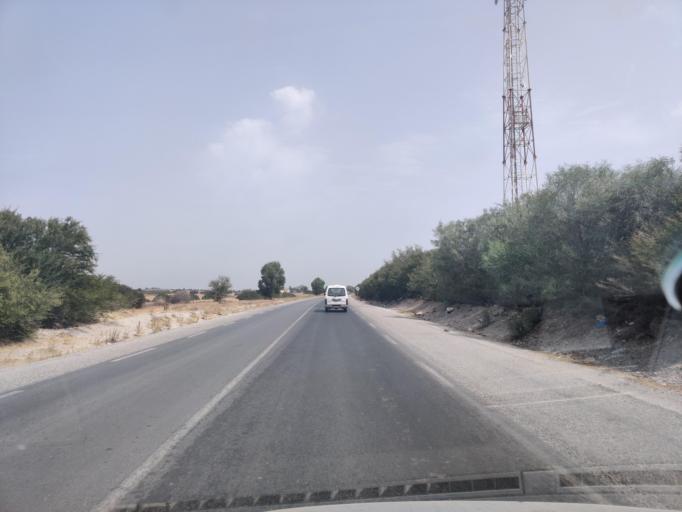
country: TN
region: Nabul
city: Bu `Urqub
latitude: 36.4809
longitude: 10.5718
